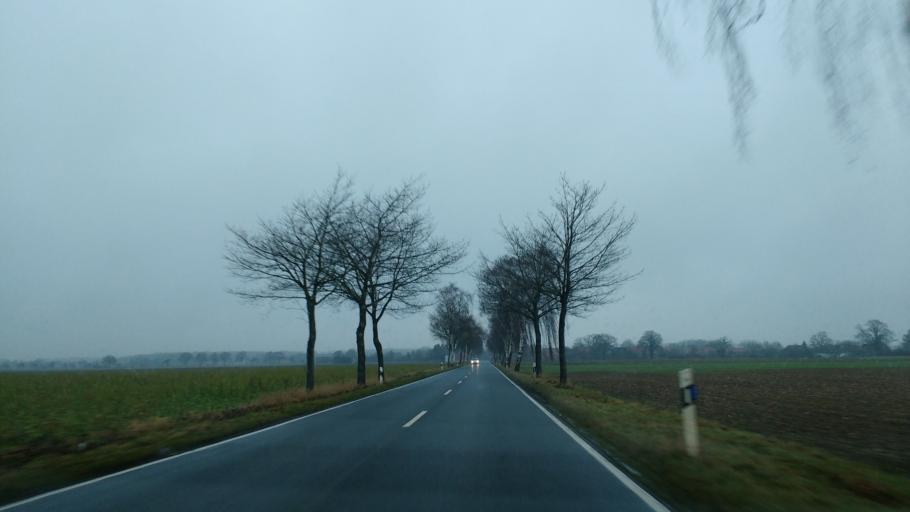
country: DE
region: Lower Saxony
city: Gilten
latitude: 52.6574
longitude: 9.5738
